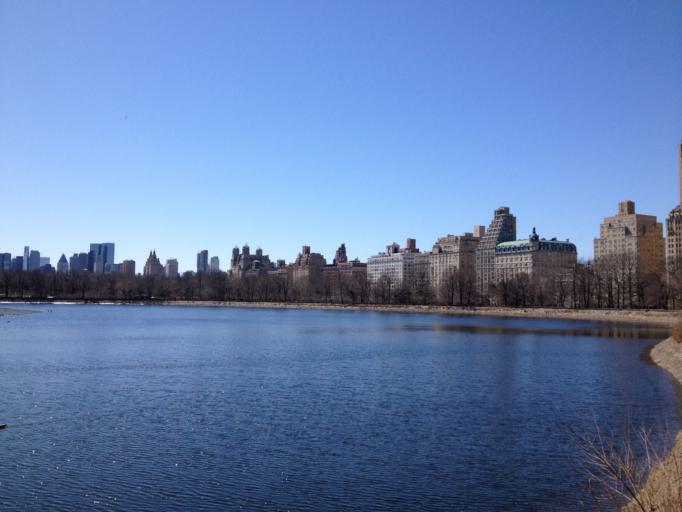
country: US
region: New York
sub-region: New York County
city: Manhattan
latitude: 40.7883
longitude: -73.9629
